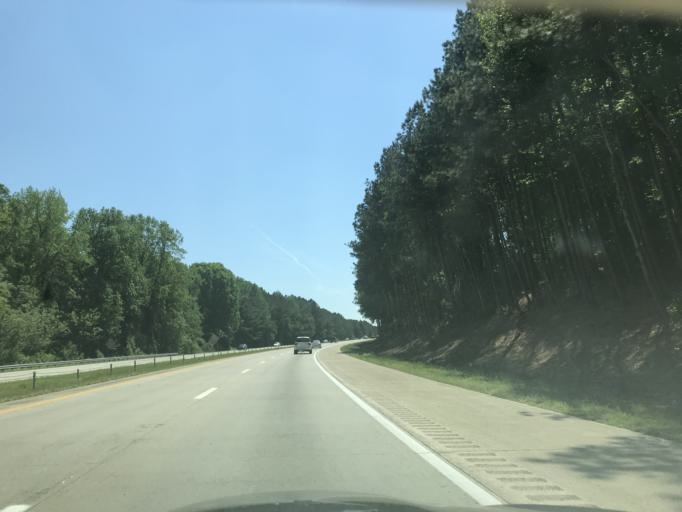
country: US
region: North Carolina
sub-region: Johnston County
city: Clayton
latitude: 35.5596
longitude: -78.5761
